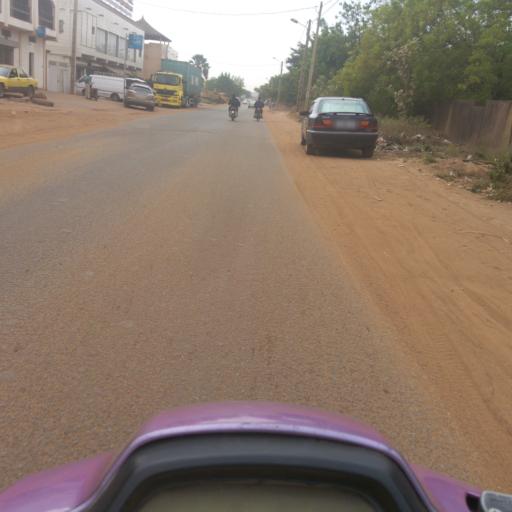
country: ML
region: Bamako
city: Bamako
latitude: 12.6615
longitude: -7.9360
